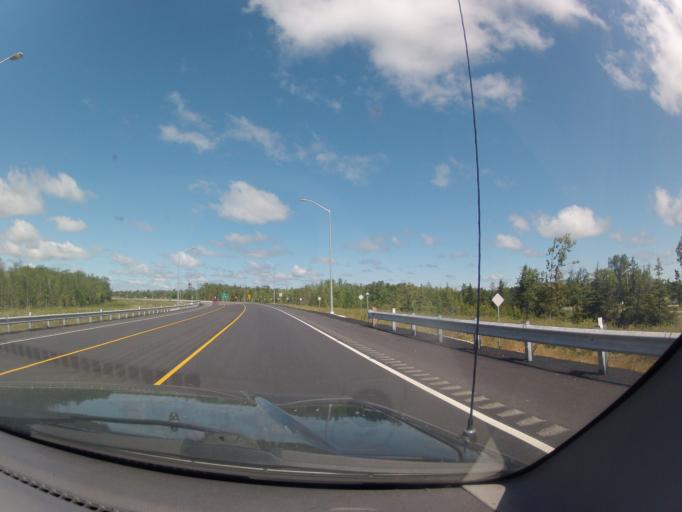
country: CA
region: Ontario
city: Wasaga Beach
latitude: 44.4587
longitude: -80.1058
